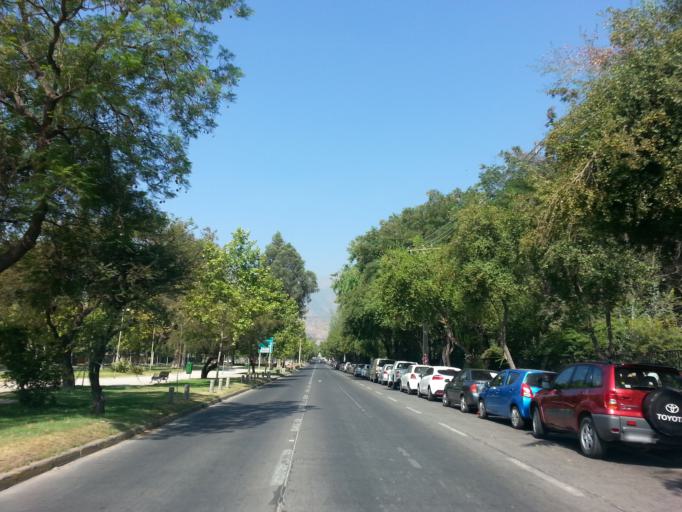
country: CL
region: Santiago Metropolitan
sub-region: Provincia de Santiago
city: Villa Presidente Frei, Nunoa, Santiago, Chile
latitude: -33.4299
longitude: -70.5464
